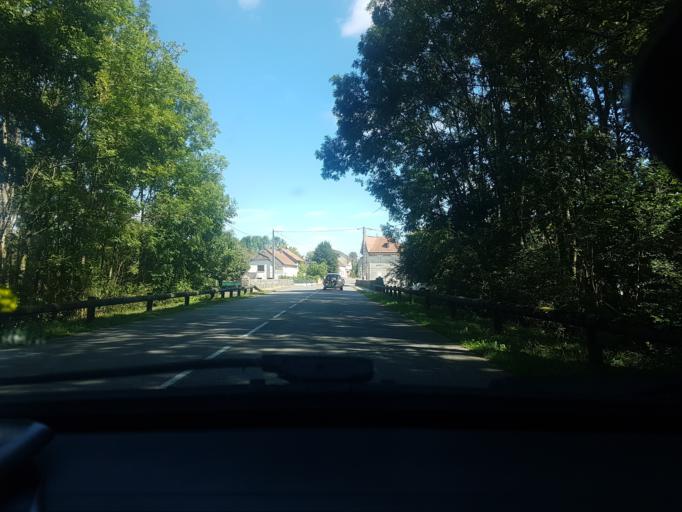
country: FR
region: Bourgogne
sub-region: Departement de la Cote-d'Or
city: Mirebeau-sur-Beze
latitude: 47.4020
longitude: 5.4034
